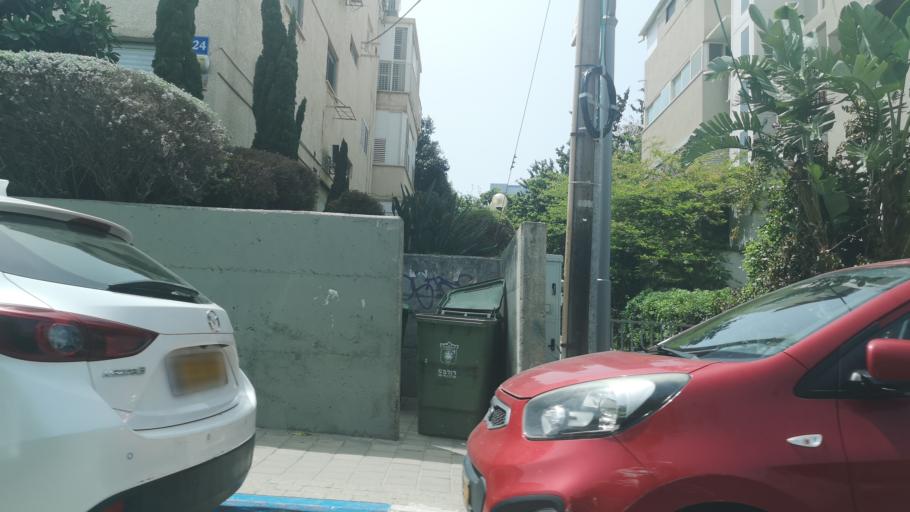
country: IL
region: Tel Aviv
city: Tel Aviv
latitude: 32.0924
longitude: 34.7753
